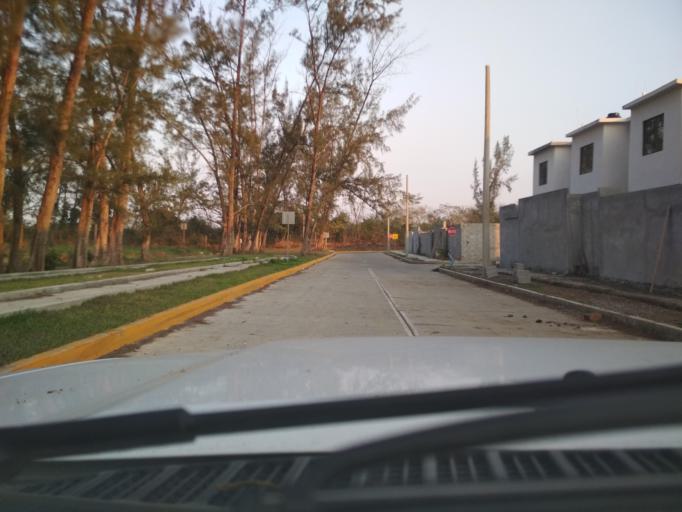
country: MX
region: Veracruz
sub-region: Veracruz
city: Las Amapolas
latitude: 19.1416
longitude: -96.2213
